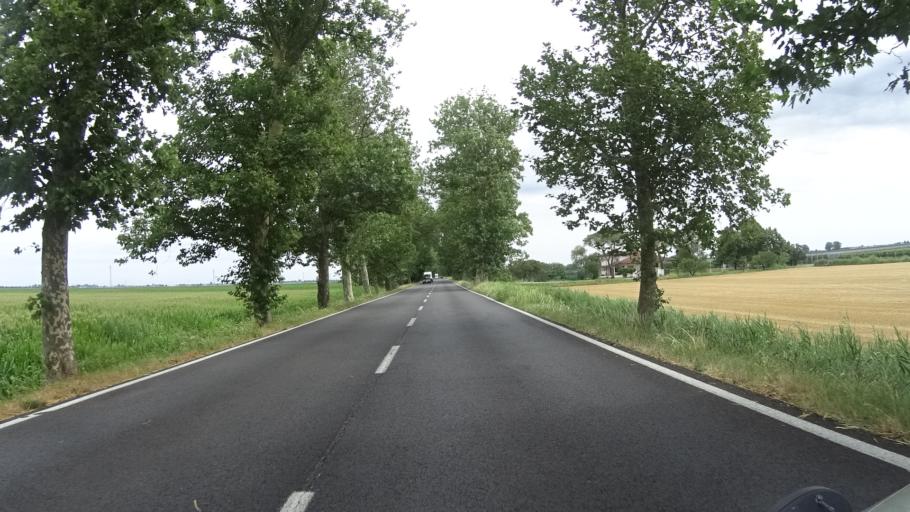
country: IT
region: Veneto
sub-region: Provincia di Venezia
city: Lugugnana
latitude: 45.7127
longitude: 12.8927
